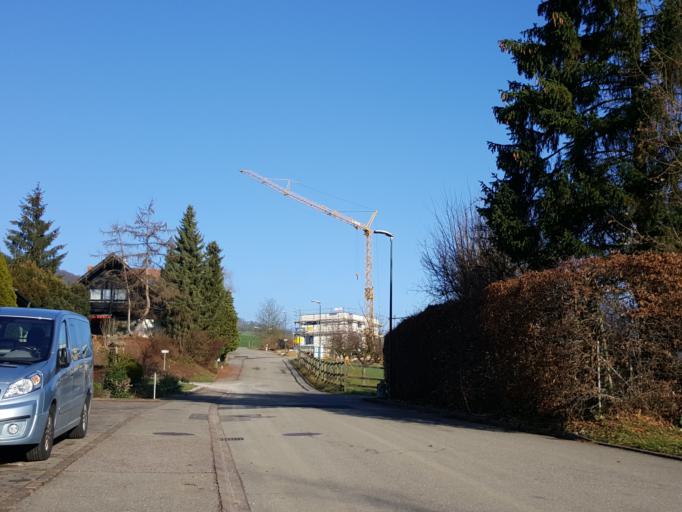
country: CH
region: Basel-Landschaft
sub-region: Bezirk Sissach
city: Ormalingen
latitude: 47.4729
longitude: 7.8746
